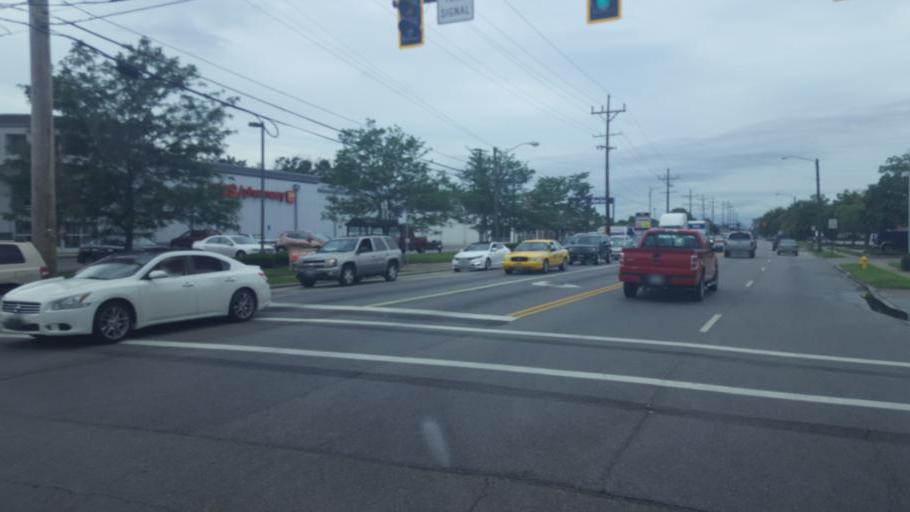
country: US
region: Ohio
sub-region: Franklin County
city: Whitehall
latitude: 39.9555
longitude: -82.8768
